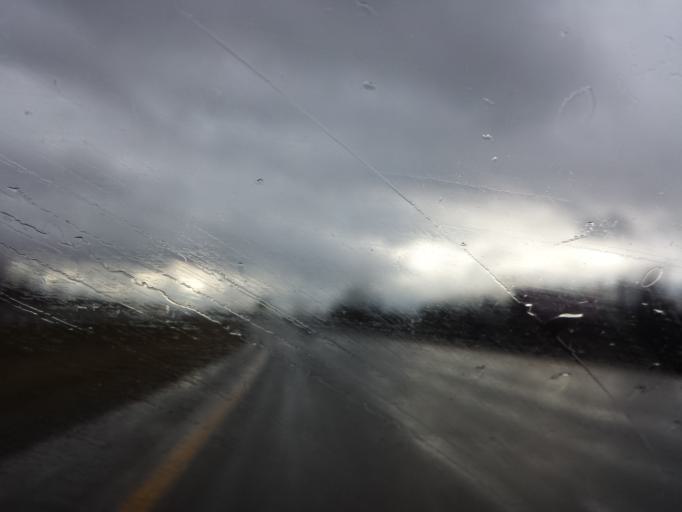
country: US
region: Michigan
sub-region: Genesee County
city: Swartz Creek
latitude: 42.9767
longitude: -83.7587
